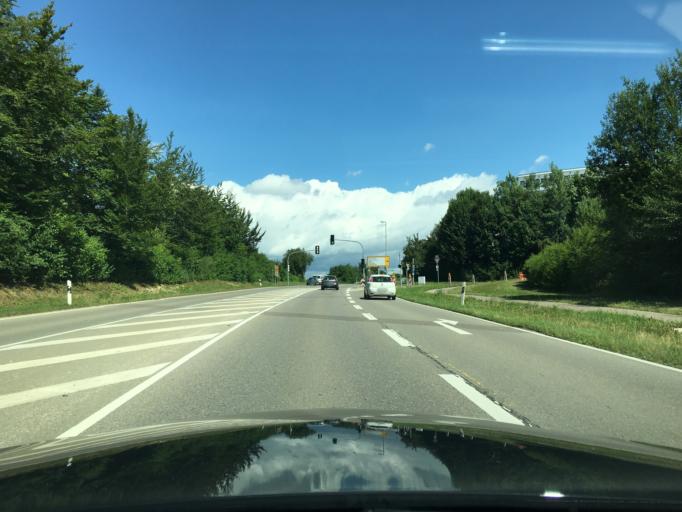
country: DE
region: Baden-Wuerttemberg
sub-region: Tuebingen Region
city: Dornstadt
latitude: 48.4179
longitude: 9.9340
